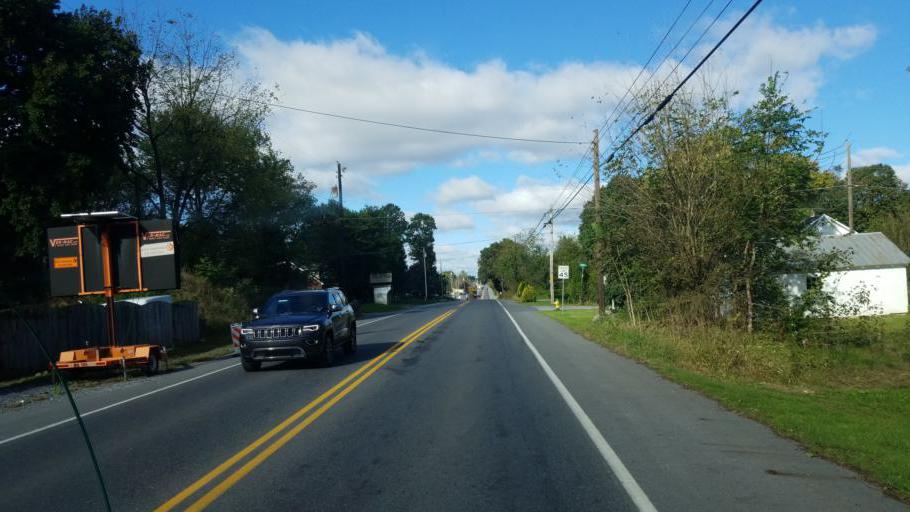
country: US
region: Pennsylvania
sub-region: Franklin County
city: Waynesboro
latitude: 39.7654
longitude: -77.6116
